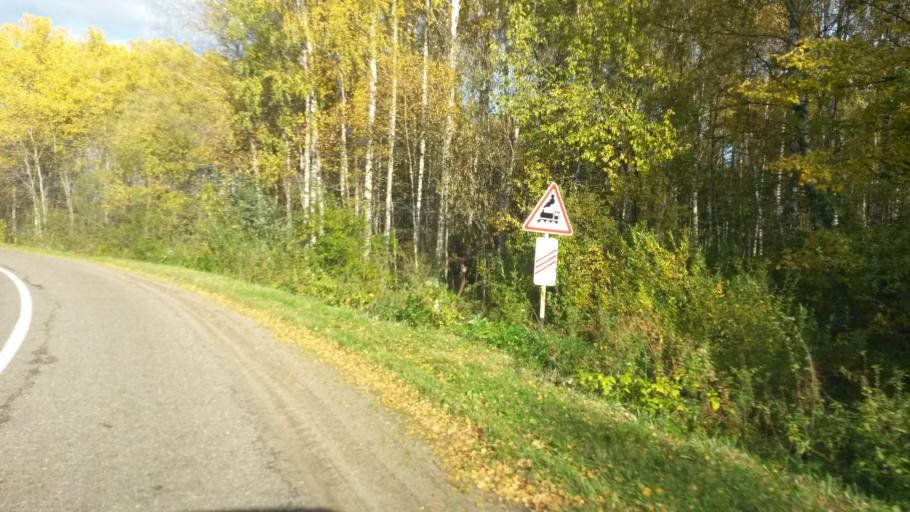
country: RU
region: Jaroslavl
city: Yaroslavl
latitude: 57.5236
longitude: 39.9735
